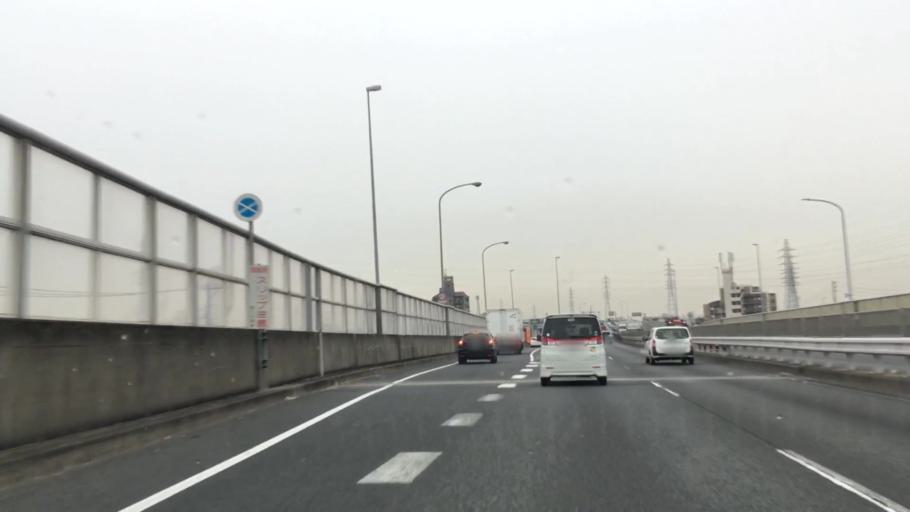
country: JP
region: Aichi
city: Chiryu
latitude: 35.0081
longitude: 137.0261
